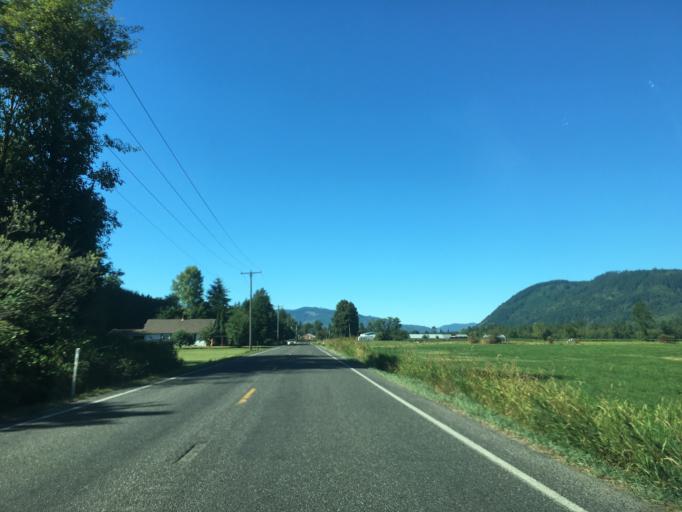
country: US
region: Washington
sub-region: Whatcom County
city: Sudden Valley
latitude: 48.7287
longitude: -122.2033
